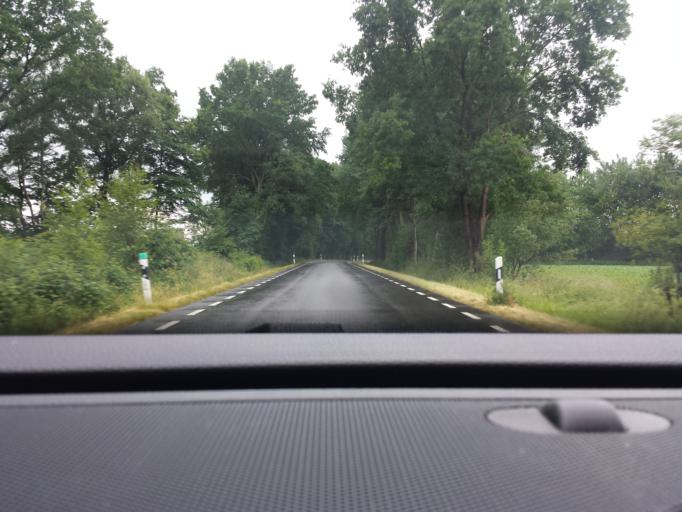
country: DE
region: North Rhine-Westphalia
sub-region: Regierungsbezirk Munster
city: Vreden
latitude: 52.0613
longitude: 6.8795
